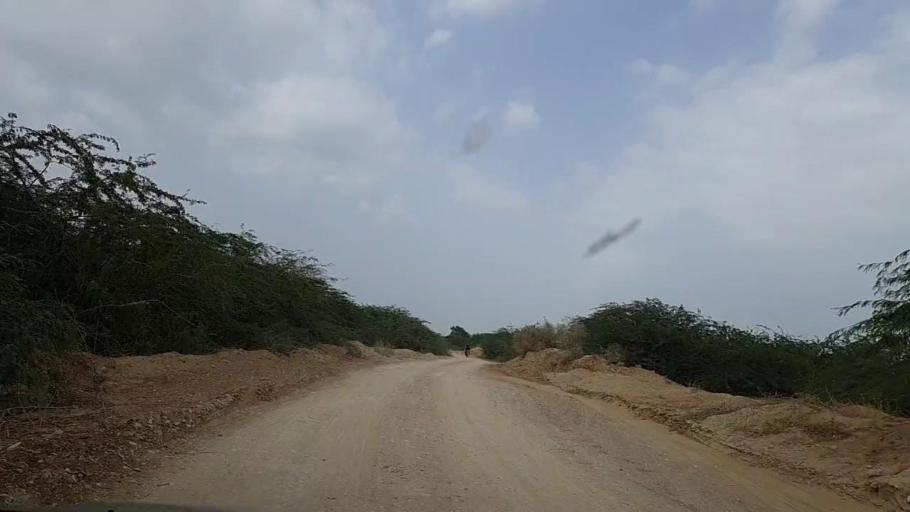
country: PK
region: Sindh
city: Kotri
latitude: 25.2798
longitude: 68.2560
